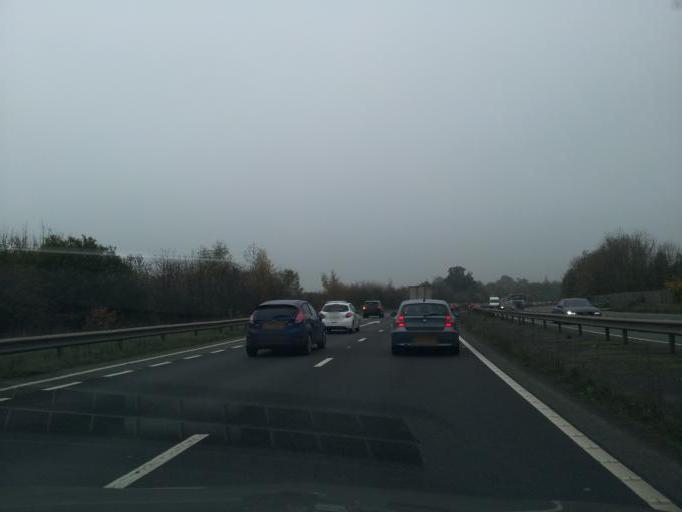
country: GB
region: England
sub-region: Leicestershire
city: Anstey
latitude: 52.6699
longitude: -1.1790
